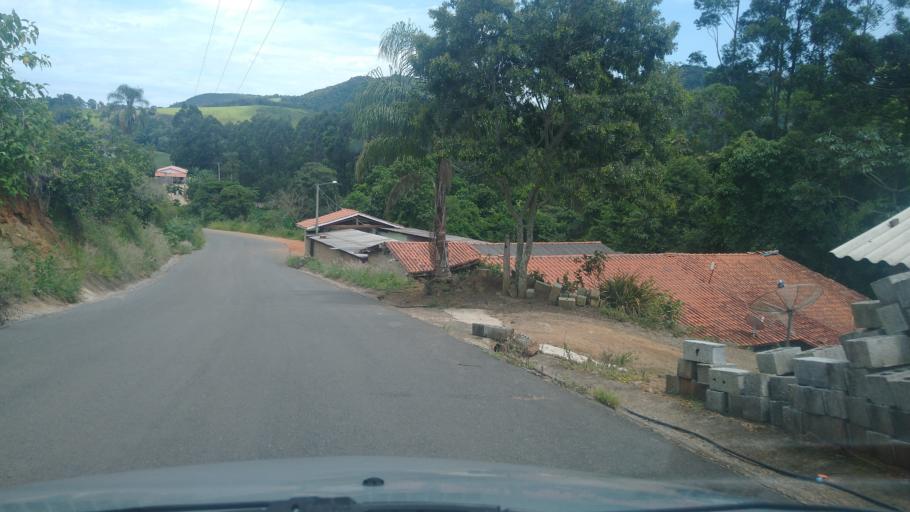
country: BR
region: Minas Gerais
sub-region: Extrema
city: Extrema
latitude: -22.7183
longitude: -46.3306
